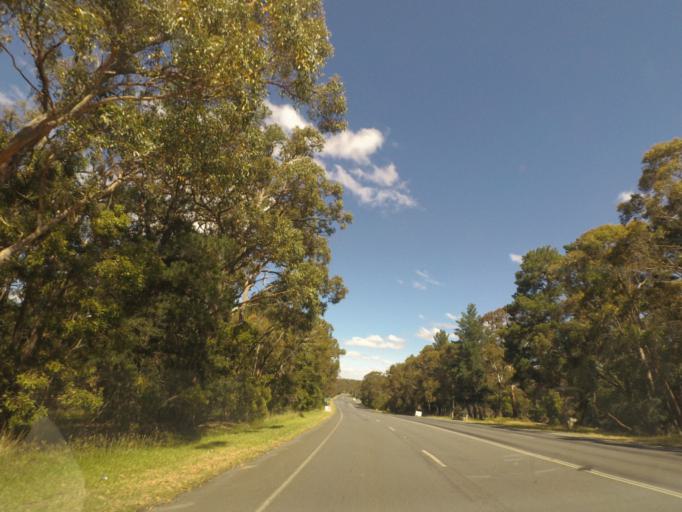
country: AU
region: Victoria
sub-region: Hume
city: Sunbury
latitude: -37.4299
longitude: 144.5558
